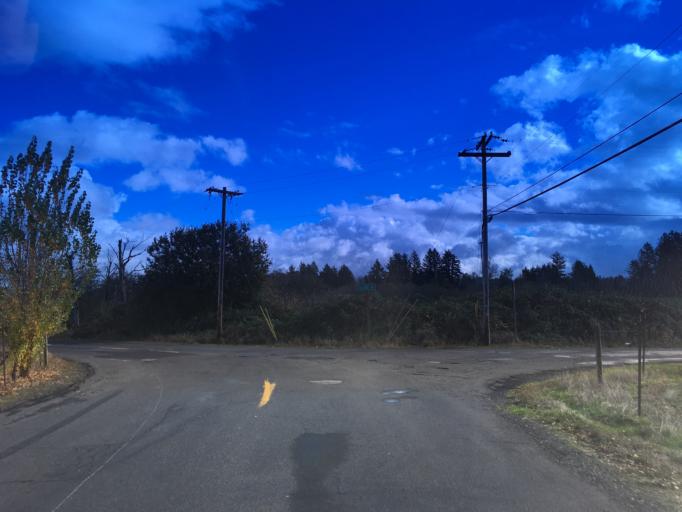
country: US
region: Oregon
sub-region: Multnomah County
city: Troutdale
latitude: 45.5065
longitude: -122.3741
